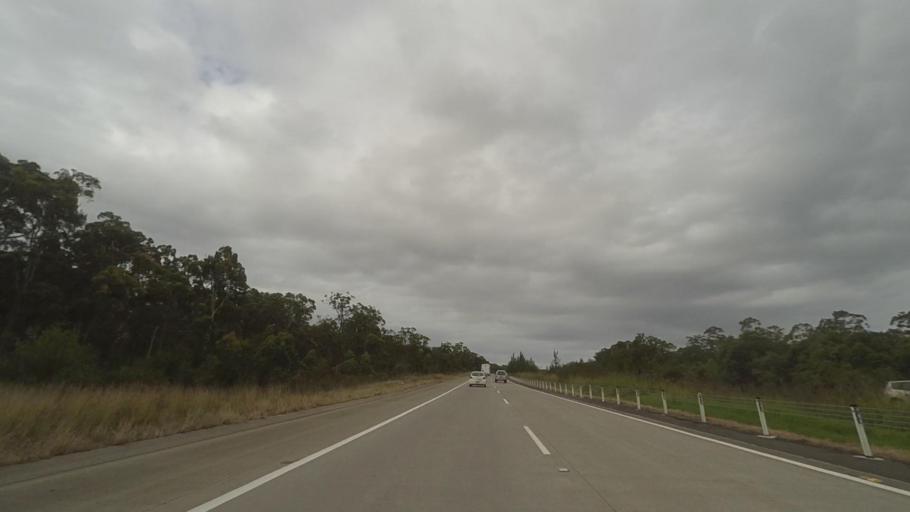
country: AU
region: New South Wales
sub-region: Port Stephens Shire
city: Port Stephens
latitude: -32.6285
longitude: 152.0519
